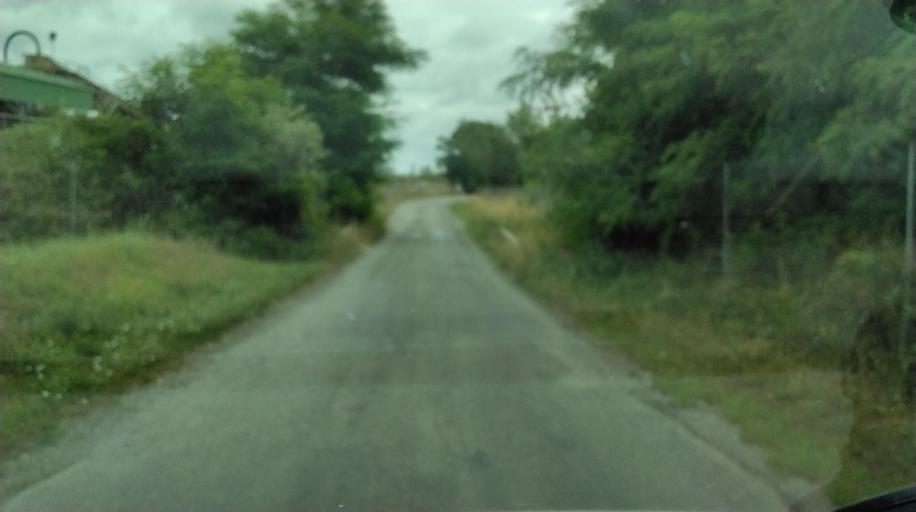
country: FR
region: Midi-Pyrenees
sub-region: Departement de la Haute-Garonne
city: Martres-Tolosane
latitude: 43.2077
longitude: 1.0413
